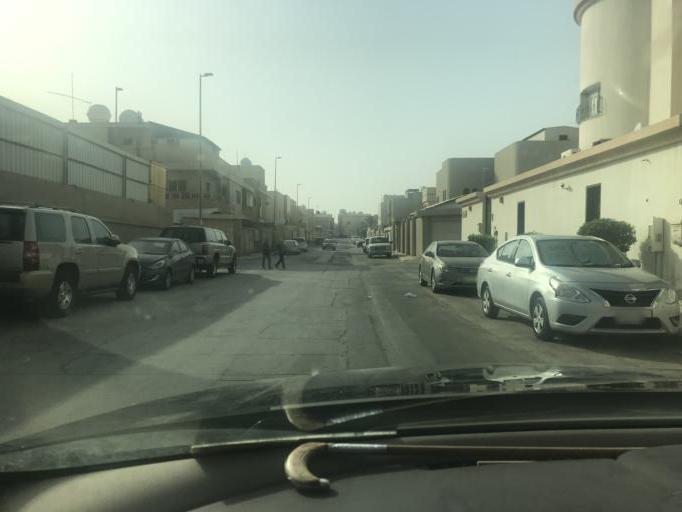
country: SA
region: Ar Riyad
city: Riyadh
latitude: 24.7202
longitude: 46.7692
